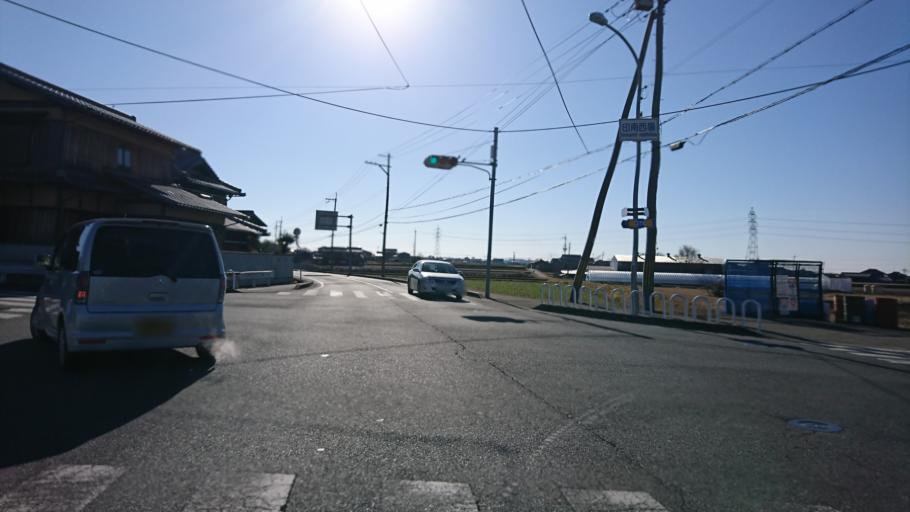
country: JP
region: Hyogo
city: Miki
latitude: 34.7374
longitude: 134.9443
